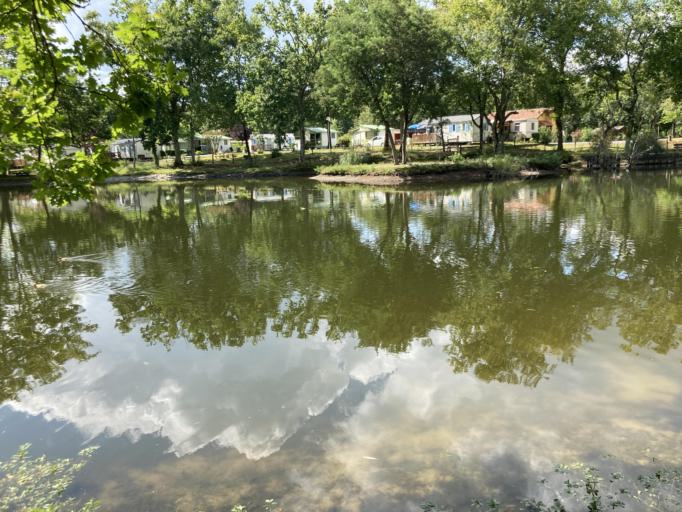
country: FR
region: Aquitaine
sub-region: Departement des Landes
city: Hinx
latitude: 43.7634
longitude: -0.8946
